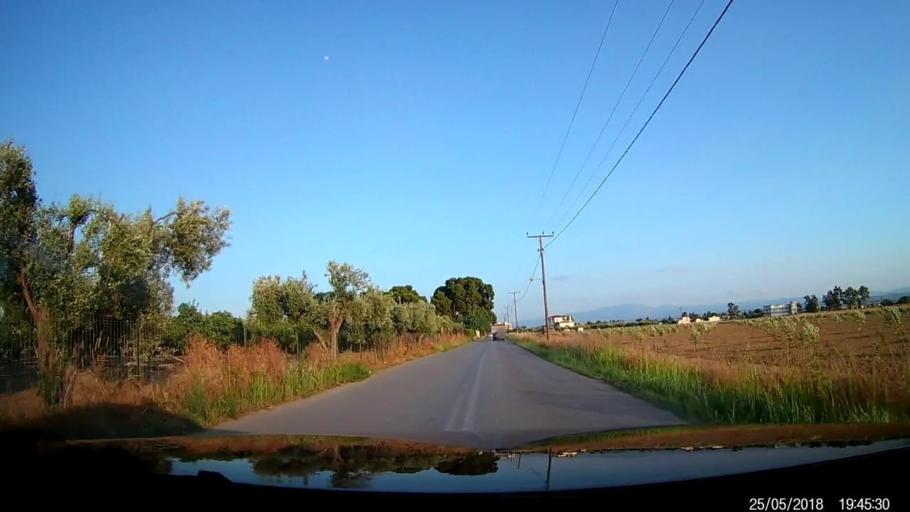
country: GR
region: Central Greece
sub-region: Nomos Evvoias
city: Ayios Nikolaos
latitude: 38.4326
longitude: 23.6335
